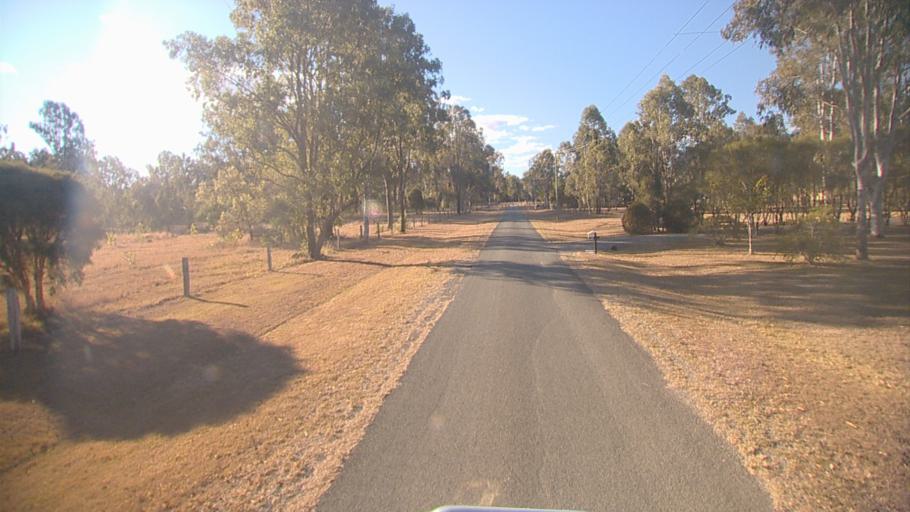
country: AU
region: Queensland
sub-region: Logan
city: Cedar Vale
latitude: -27.8438
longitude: 153.0139
